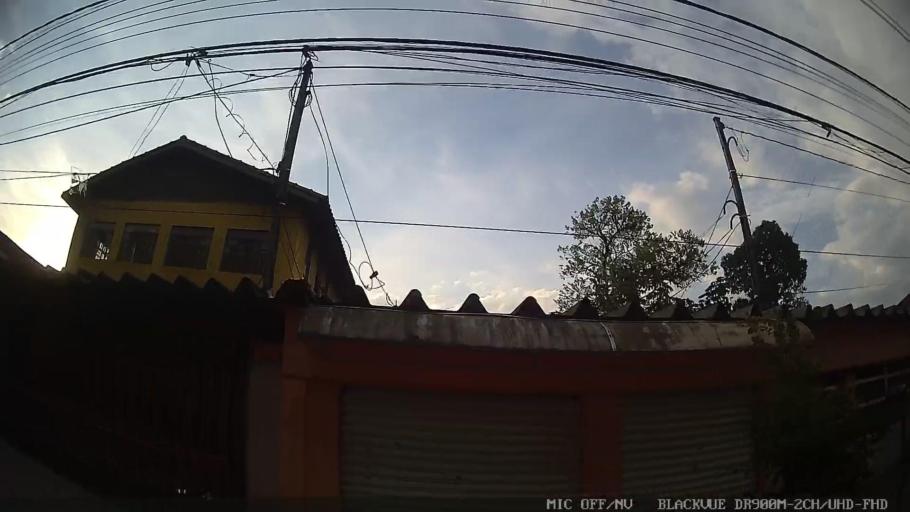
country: BR
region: Sao Paulo
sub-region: Cubatao
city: Cubatao
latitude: -23.8930
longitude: -46.4299
